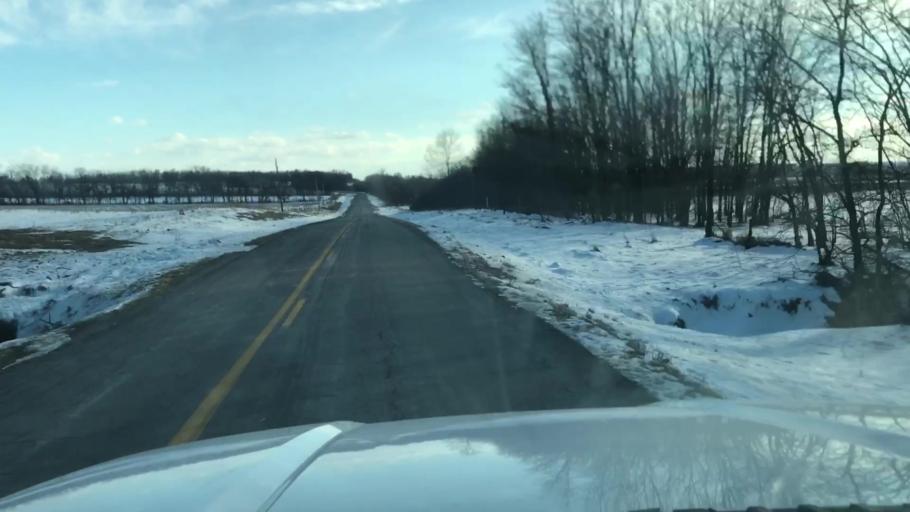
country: US
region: Missouri
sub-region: Holt County
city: Oregon
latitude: 40.1099
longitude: -95.0226
